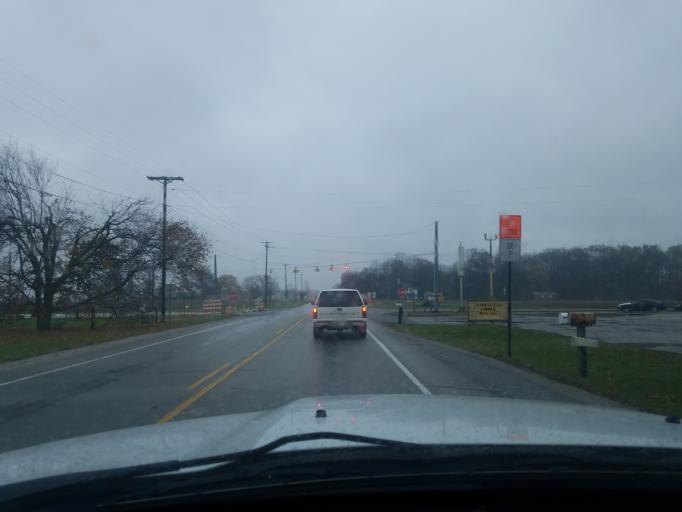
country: US
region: Indiana
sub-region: Grant County
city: Fairmount
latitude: 40.4225
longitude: -85.6728
